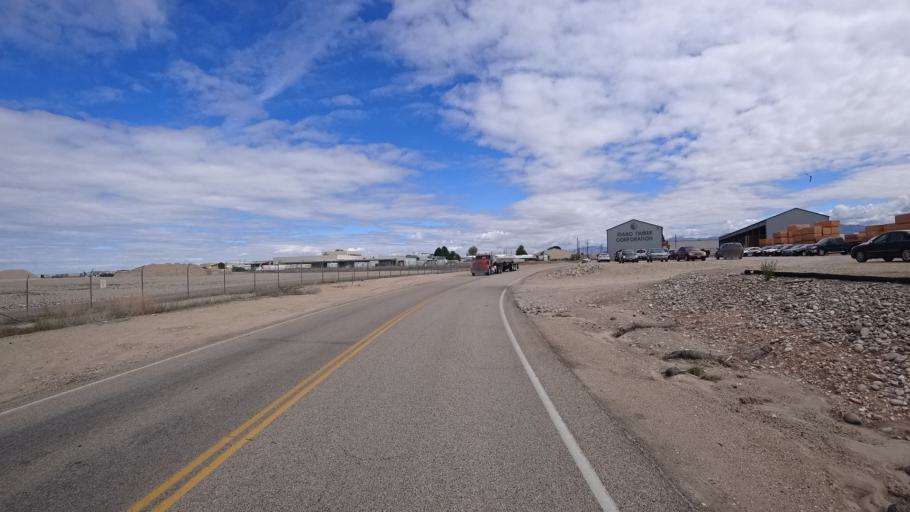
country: US
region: Idaho
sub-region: Ada County
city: Boise
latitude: 43.5573
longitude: -116.1937
